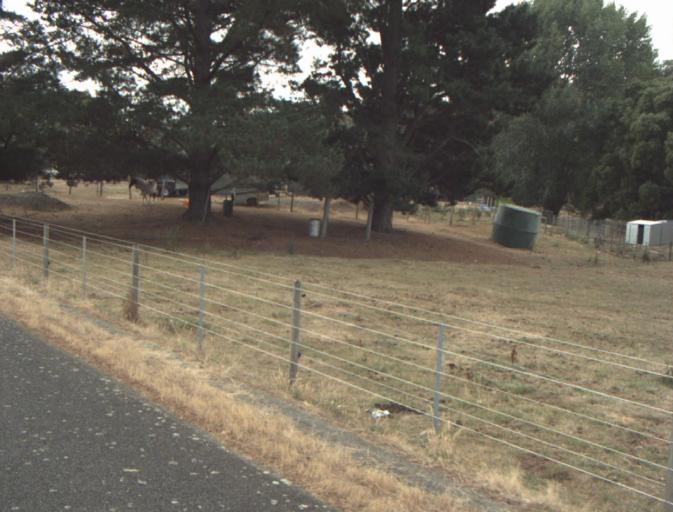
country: AU
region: Tasmania
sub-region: Launceston
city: Mayfield
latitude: -41.2921
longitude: 147.0207
